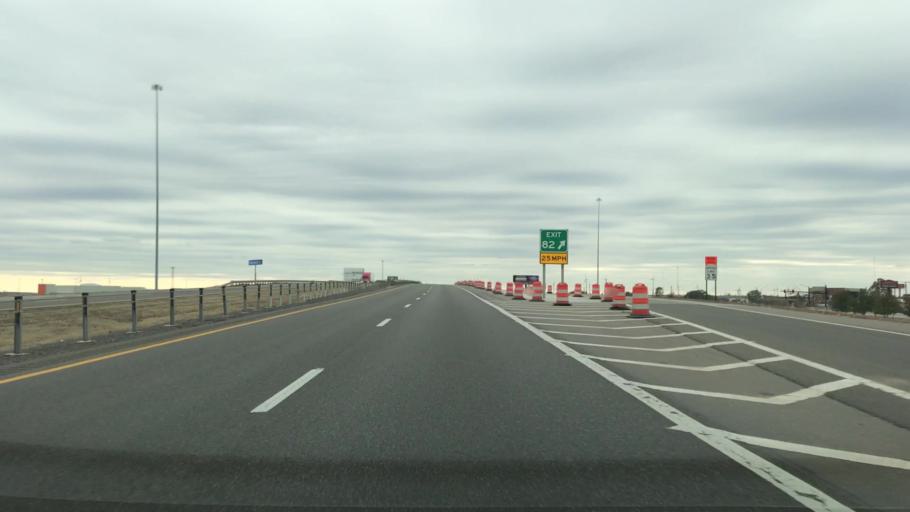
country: US
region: Oklahoma
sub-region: Custer County
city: Weatherford
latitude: 35.5284
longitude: -98.6889
